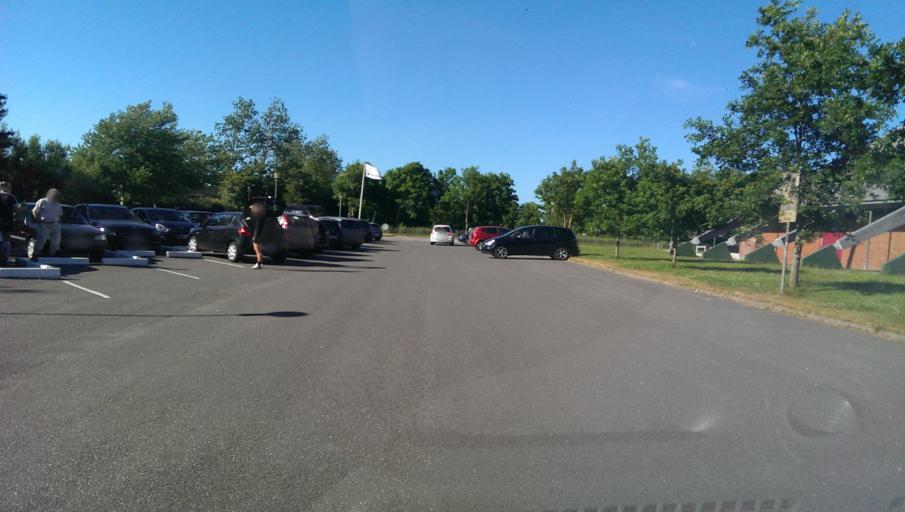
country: DK
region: South Denmark
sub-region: Esbjerg Kommune
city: Esbjerg
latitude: 55.5201
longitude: 8.3975
